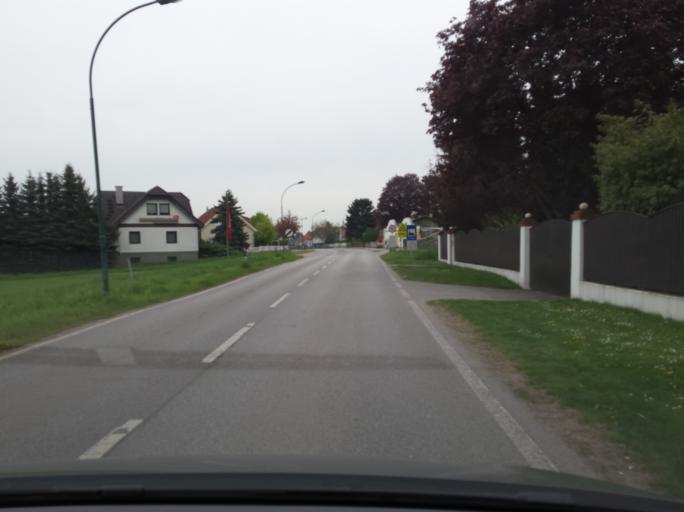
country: AT
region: Lower Austria
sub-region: Politischer Bezirk Bruck an der Leitha
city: Bruck an der Leitha
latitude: 48.0322
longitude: 16.7692
